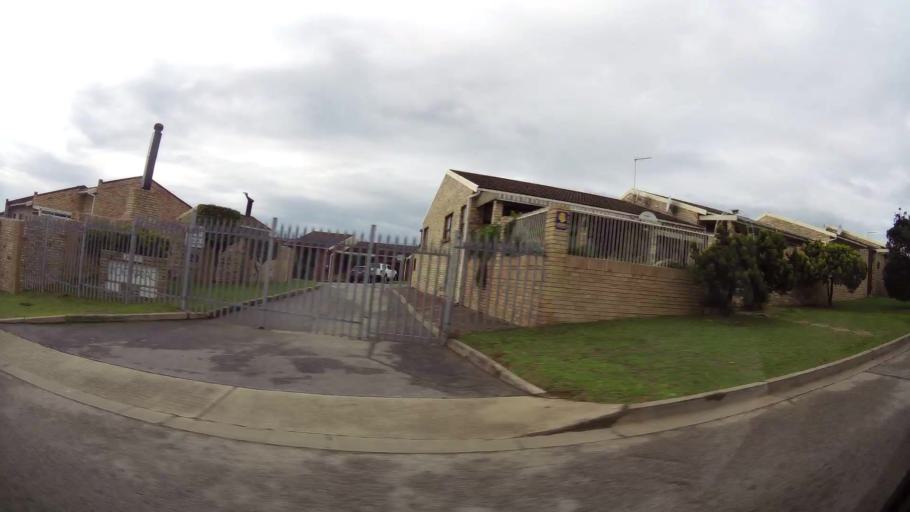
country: ZA
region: Eastern Cape
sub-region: Nelson Mandela Bay Metropolitan Municipality
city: Port Elizabeth
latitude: -33.9674
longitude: 25.6248
